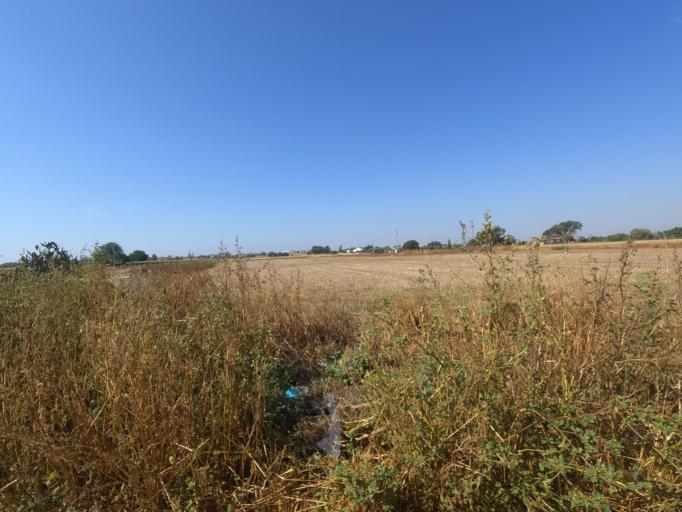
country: CY
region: Ammochostos
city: Frenaros
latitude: 35.0381
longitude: 33.9411
